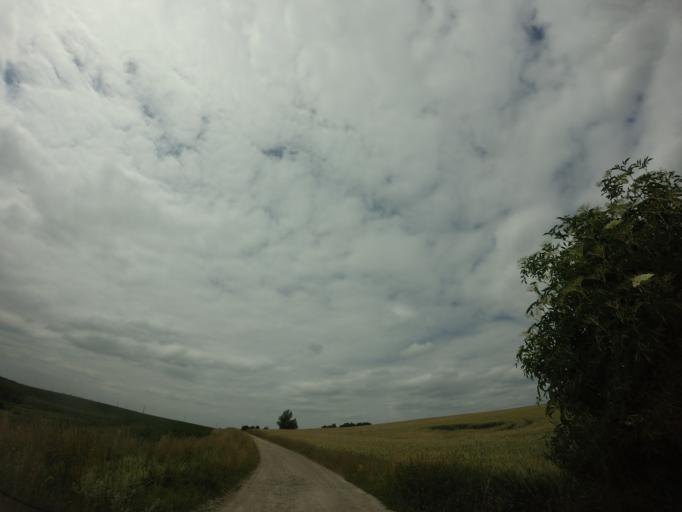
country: PL
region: West Pomeranian Voivodeship
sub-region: Powiat choszczenski
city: Krzecin
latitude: 53.0788
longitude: 15.5206
